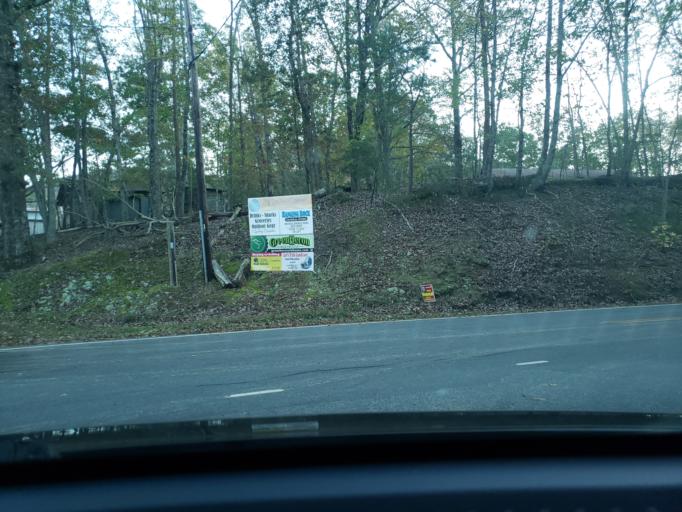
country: US
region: North Carolina
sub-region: Stokes County
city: Danbury
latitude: 36.4149
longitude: -80.2452
